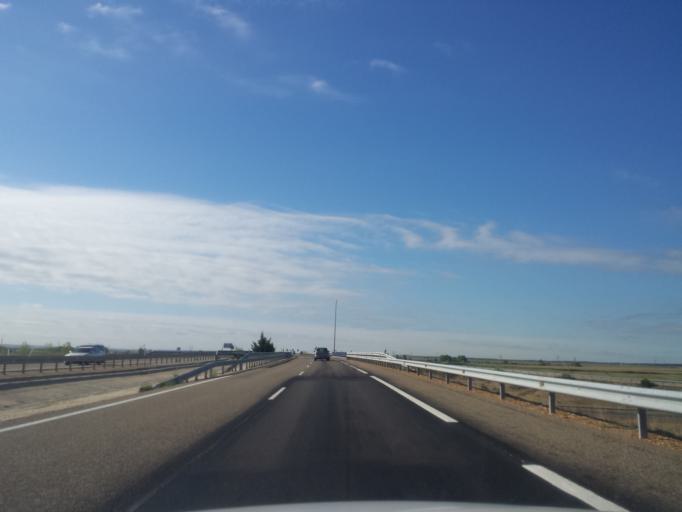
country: ES
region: Castille and Leon
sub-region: Provincia de Leon
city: Villamanan
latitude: 42.3273
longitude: -5.6094
